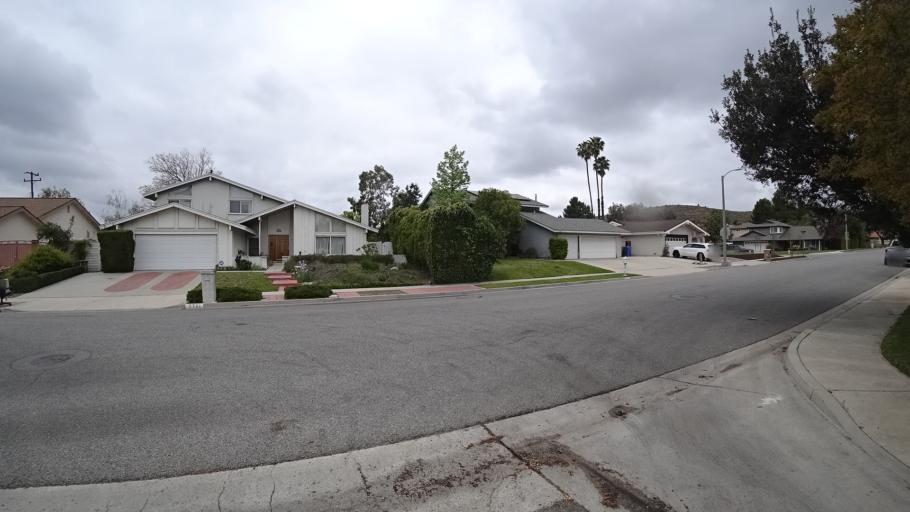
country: US
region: California
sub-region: Ventura County
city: Thousand Oaks
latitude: 34.2164
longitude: -118.8827
